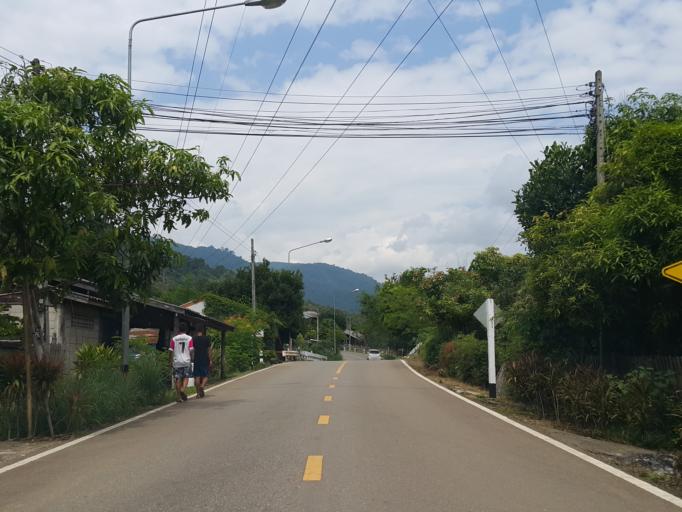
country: TH
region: Mae Hong Son
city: Mae Hong Son
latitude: 19.4685
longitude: 97.9672
